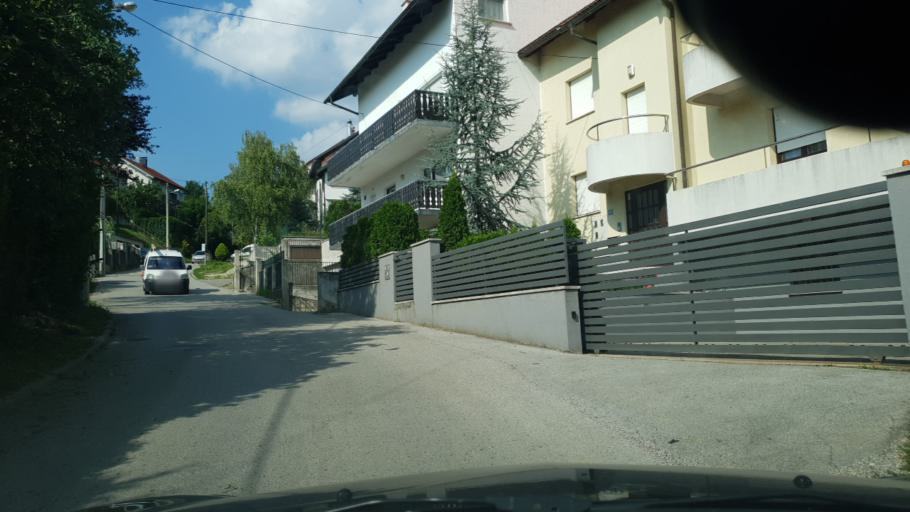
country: HR
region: Grad Zagreb
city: Stenjevec
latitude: 45.8402
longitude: 15.9240
